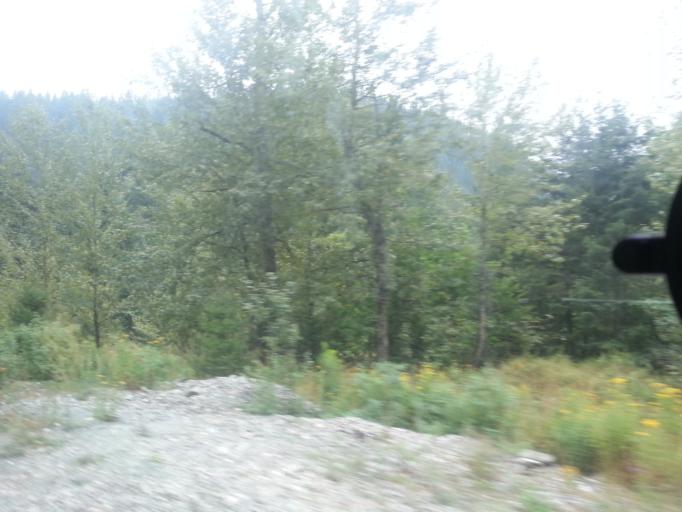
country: CA
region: British Columbia
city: Hope
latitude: 49.7152
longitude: -121.4199
